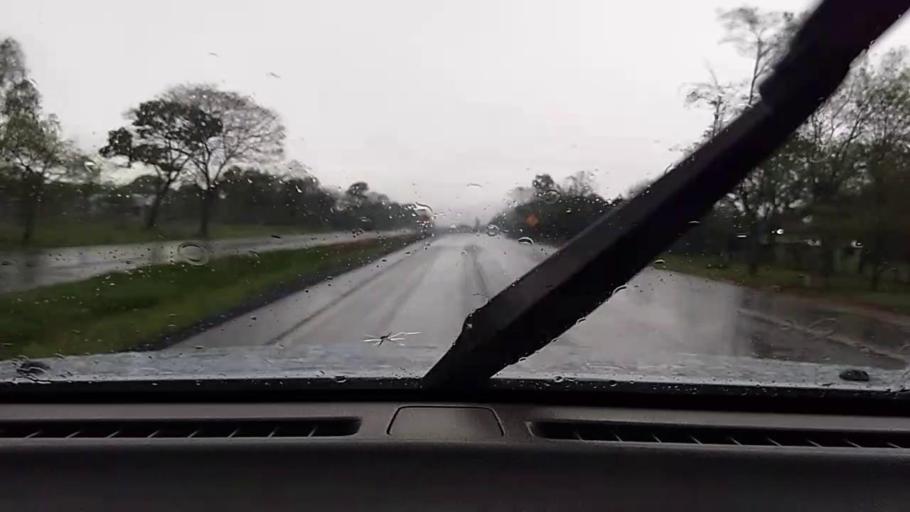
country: PY
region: Caaguazu
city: Repatriacion
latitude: -25.4534
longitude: -55.9075
